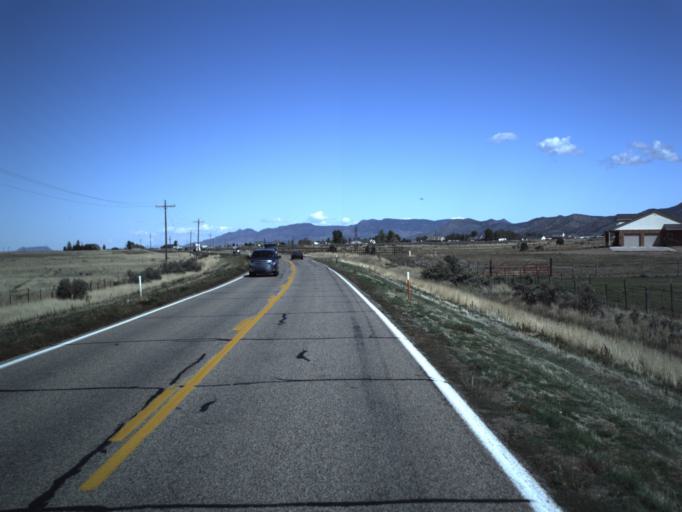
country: US
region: Utah
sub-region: Washington County
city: Enterprise
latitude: 37.5908
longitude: -113.6687
